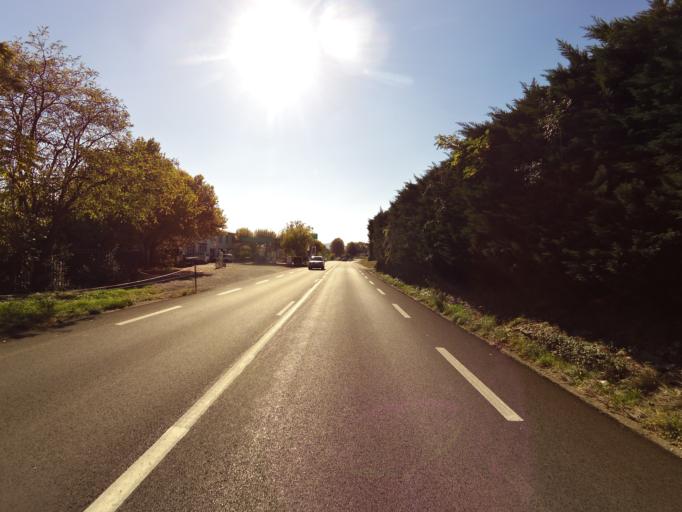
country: FR
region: Rhone-Alpes
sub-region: Departement de l'Ardeche
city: Saint-Privat
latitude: 44.6327
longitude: 4.4220
